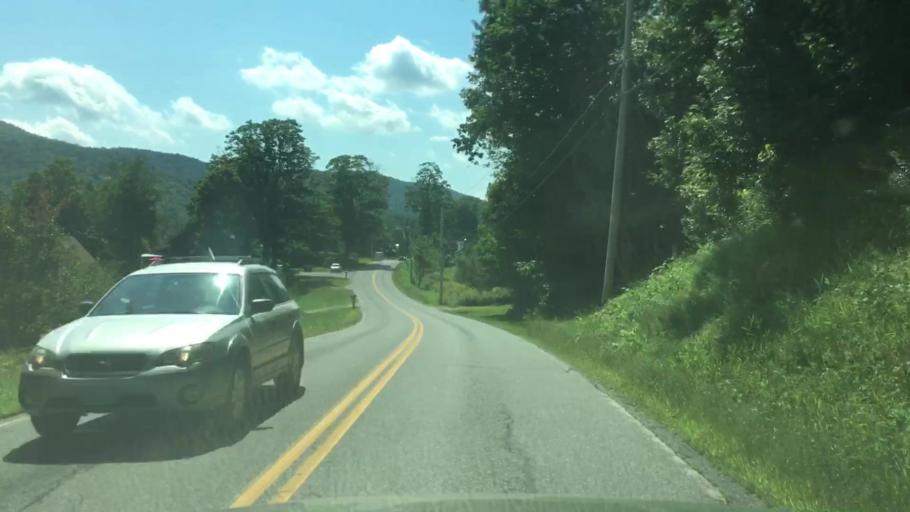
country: US
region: Vermont
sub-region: Windham County
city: West Brattleboro
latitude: 42.7966
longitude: -72.5987
